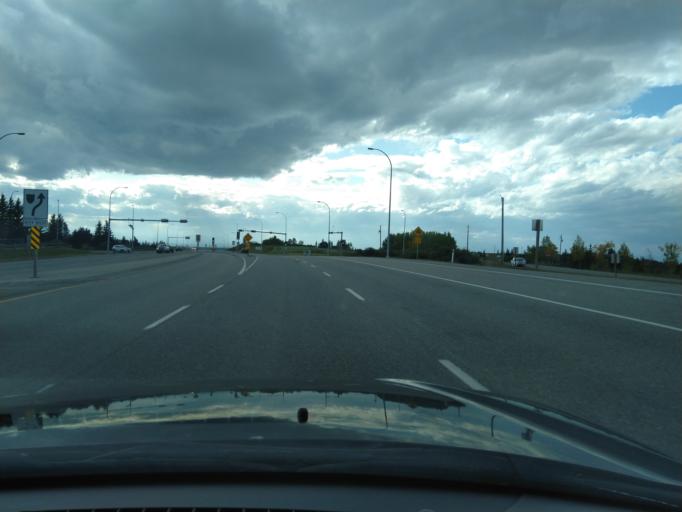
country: CA
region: Alberta
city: Cochrane
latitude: 51.1973
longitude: -114.4215
